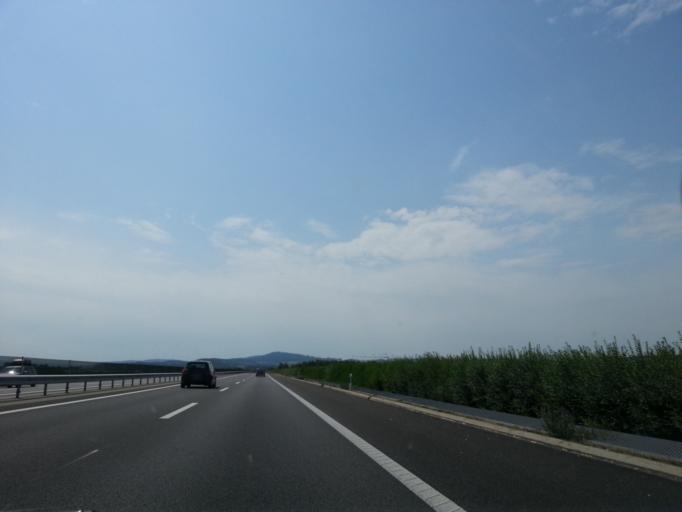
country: CH
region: Vaud
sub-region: Broye-Vully District
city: Payerne
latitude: 46.8508
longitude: 6.9395
